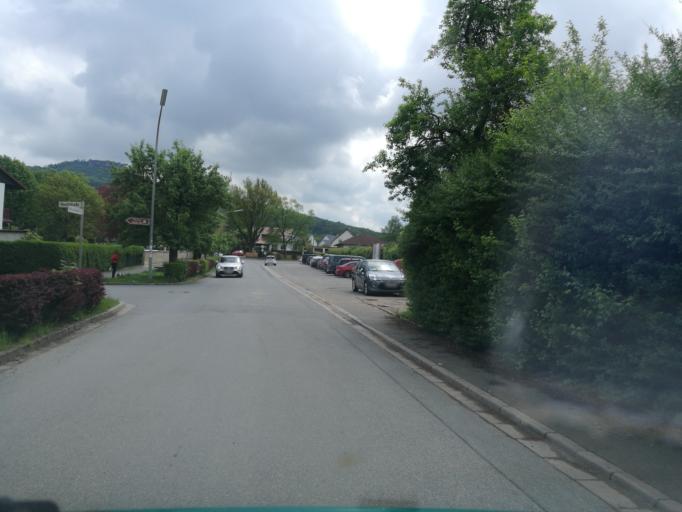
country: DE
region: Bavaria
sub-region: Upper Franconia
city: Bad Staffelstein
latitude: 50.1007
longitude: 11.0035
